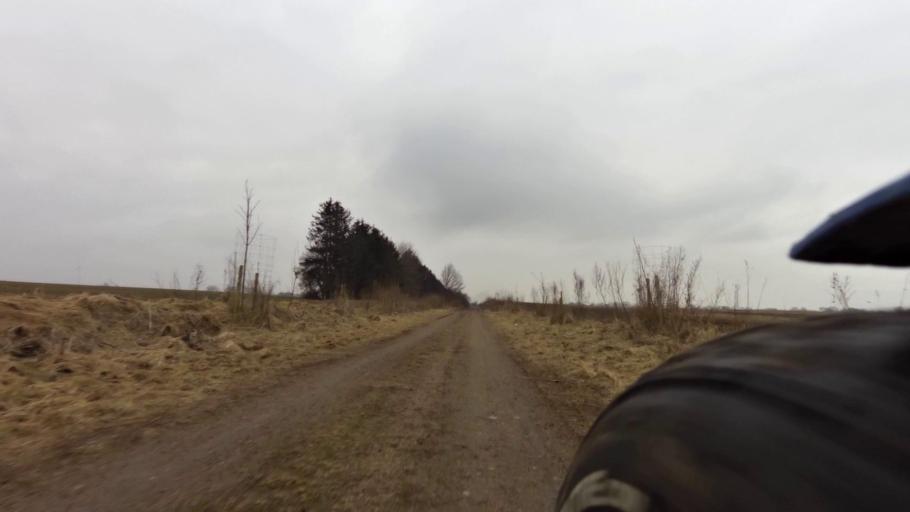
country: PL
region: West Pomeranian Voivodeship
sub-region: Powiat walecki
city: Walcz
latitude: 53.2386
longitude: 16.4641
